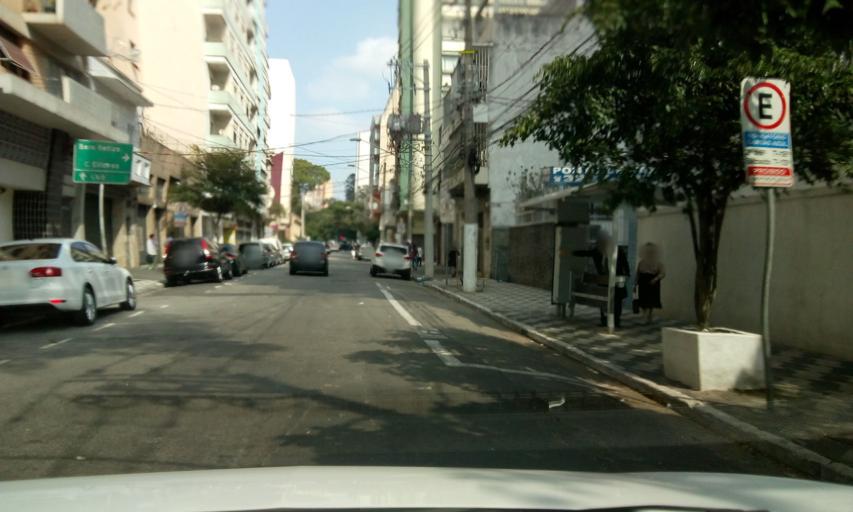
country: BR
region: Sao Paulo
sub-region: Sao Paulo
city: Sao Paulo
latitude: -23.5283
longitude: -46.6336
